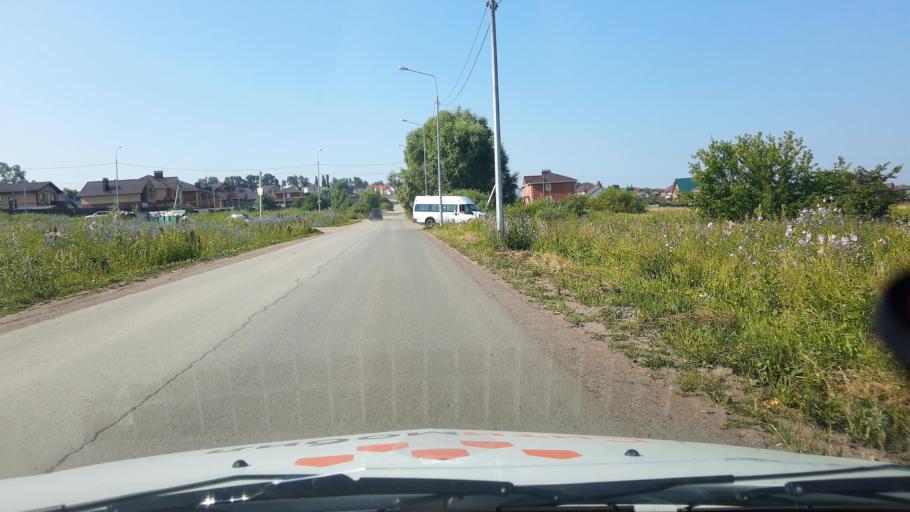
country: RU
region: Bashkortostan
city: Kabakovo
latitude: 54.6380
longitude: 56.0762
